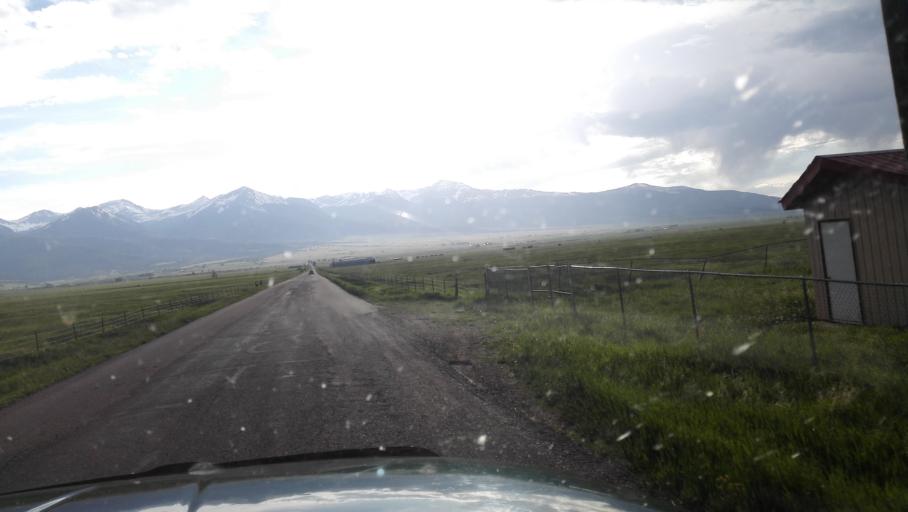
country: US
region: Colorado
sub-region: Custer County
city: Westcliffe
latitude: 38.1312
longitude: -105.4734
